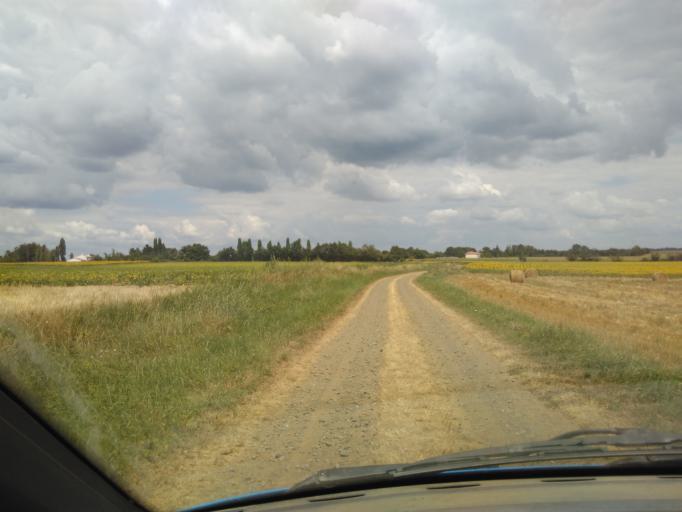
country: FR
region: Pays de la Loire
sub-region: Departement de la Vendee
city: Sainte-Hermine
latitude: 46.5726
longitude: -1.0244
